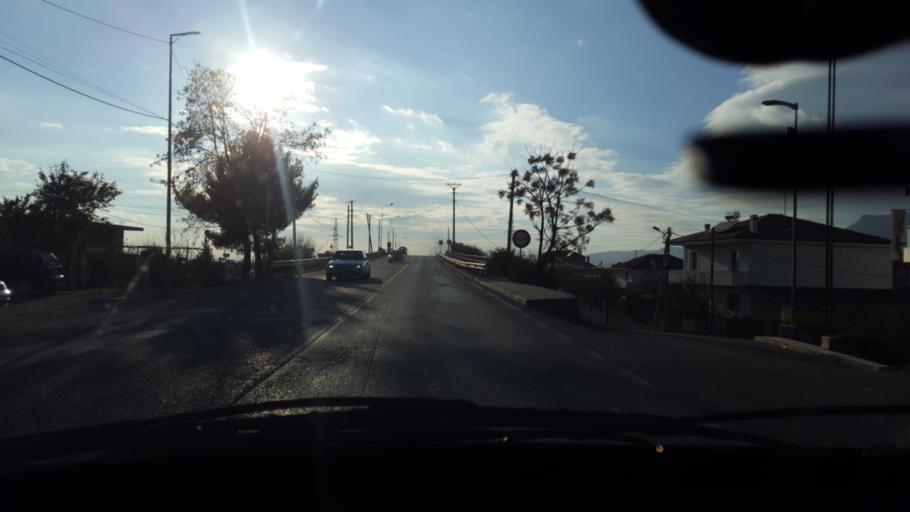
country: AL
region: Elbasan
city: Elbasan
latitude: 41.1059
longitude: 20.0636
